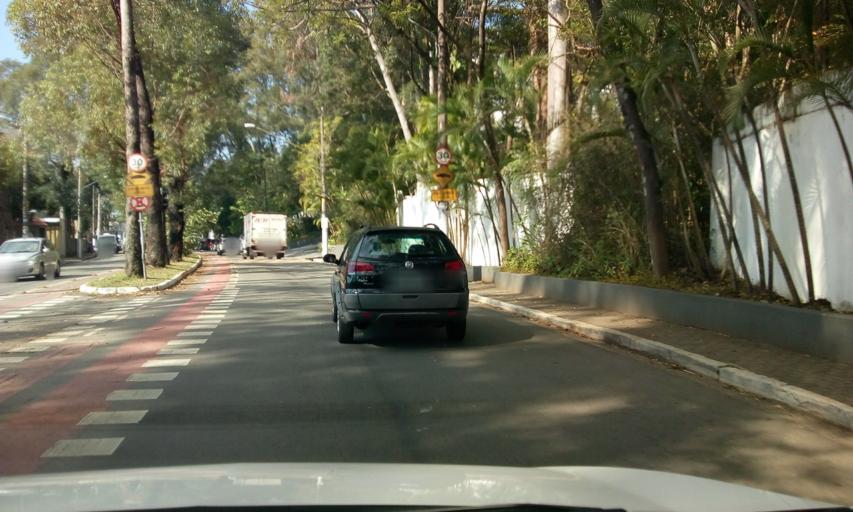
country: BR
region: Sao Paulo
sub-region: Osasco
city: Osasco
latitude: -23.5588
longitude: -46.7594
